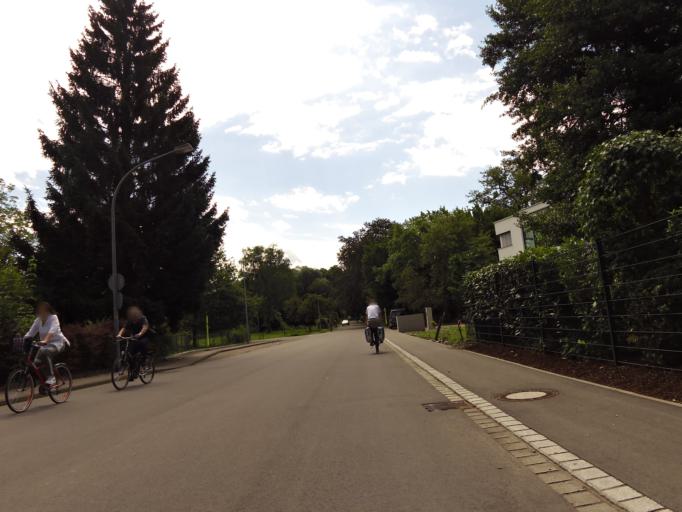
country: AT
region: Vorarlberg
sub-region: Politischer Bezirk Bregenz
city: Horbranz
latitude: 47.5480
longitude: 9.7194
